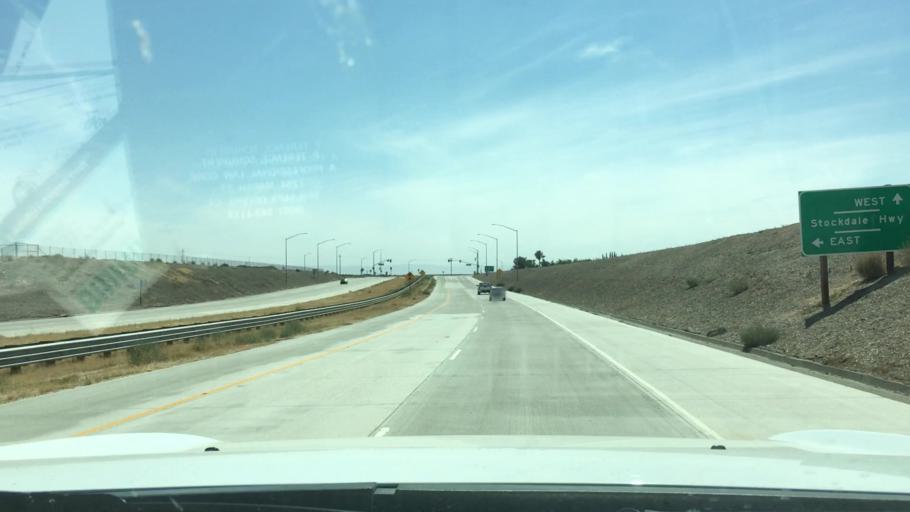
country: US
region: California
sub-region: Kern County
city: Rosedale
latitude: 35.3577
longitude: -119.1717
